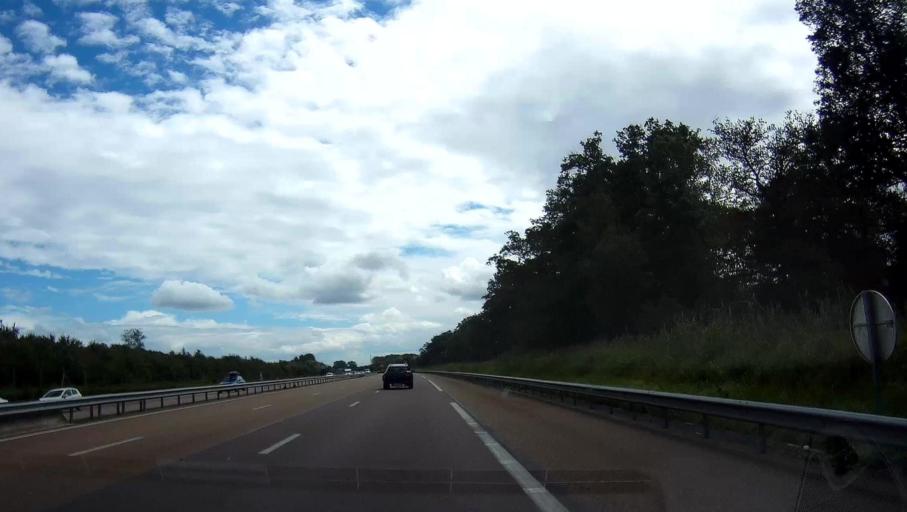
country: FR
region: Bourgogne
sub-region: Departement de la Cote-d'Or
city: Saint-Julien
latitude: 47.4157
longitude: 5.1757
